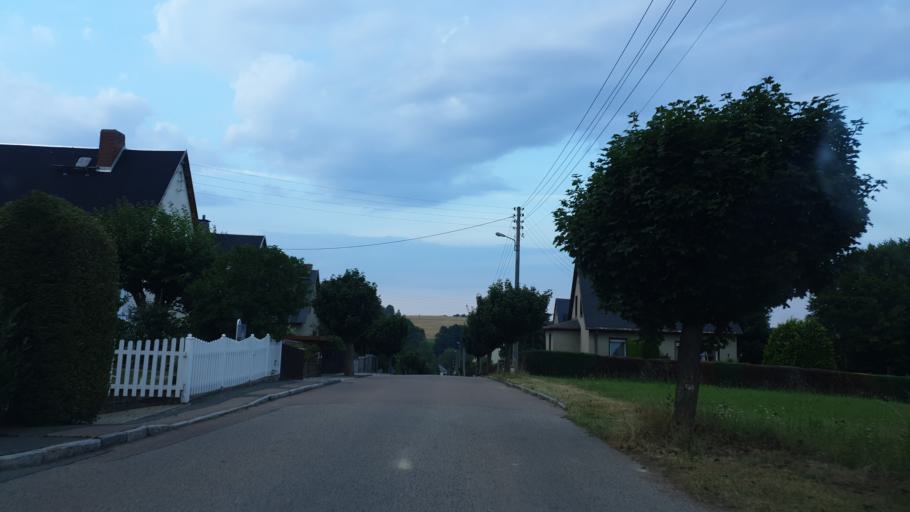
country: DE
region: Saxony
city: Gersdorf
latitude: 50.7377
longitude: 12.7284
